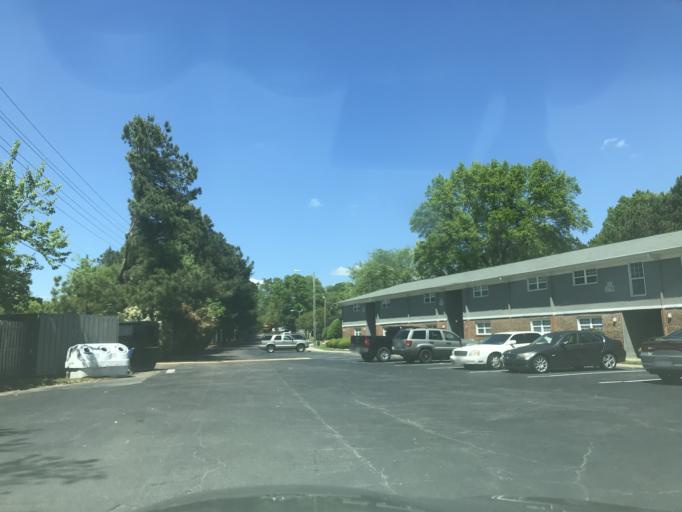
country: US
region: North Carolina
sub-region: Wake County
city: Raleigh
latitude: 35.8463
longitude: -78.5781
